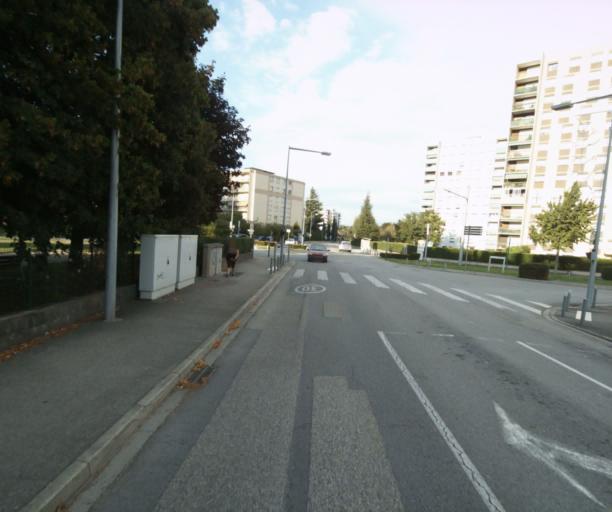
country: FR
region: Rhone-Alpes
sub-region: Departement de l'Isere
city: Seyssinet-Pariset
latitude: 45.1705
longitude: 5.6938
